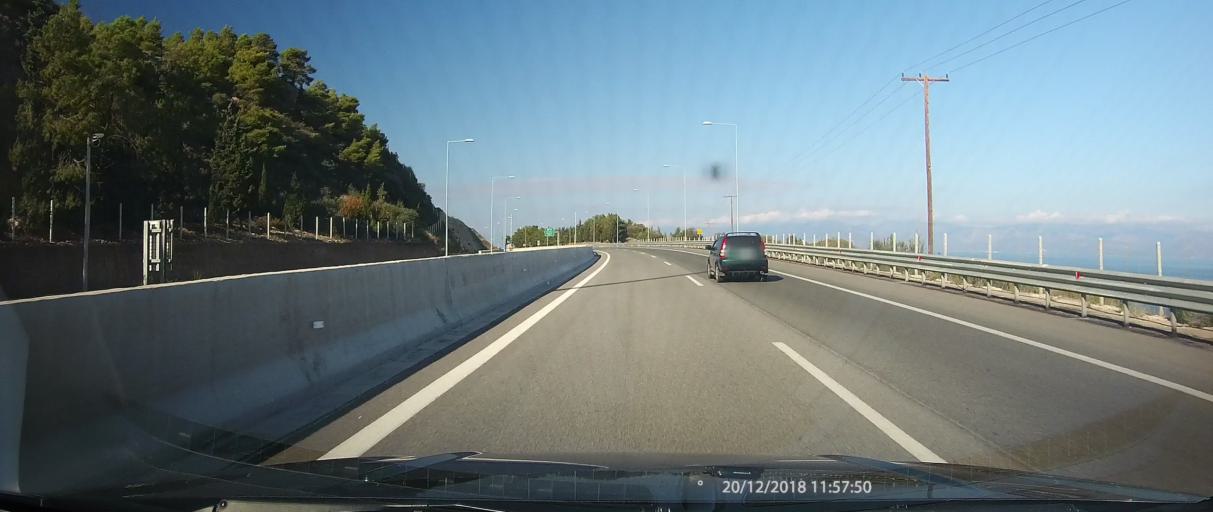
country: GR
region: West Greece
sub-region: Nomos Achaias
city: Akrata
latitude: 38.1714
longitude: 22.2602
